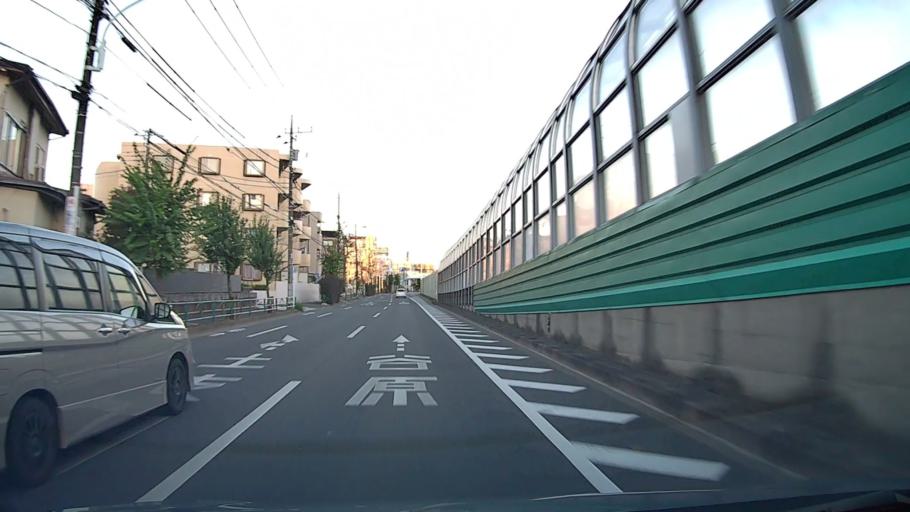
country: JP
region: Saitama
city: Wako
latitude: 35.7553
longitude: 139.6053
